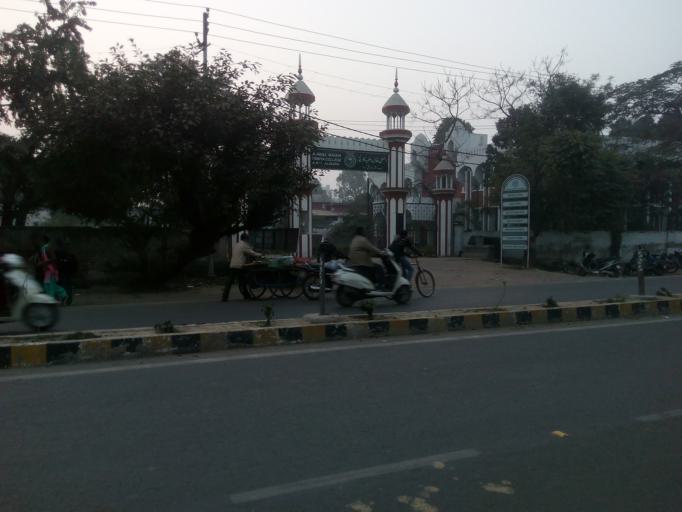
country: IN
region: Uttar Pradesh
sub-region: Aligarh
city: Aligarh
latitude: 27.8980
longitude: 78.0730
